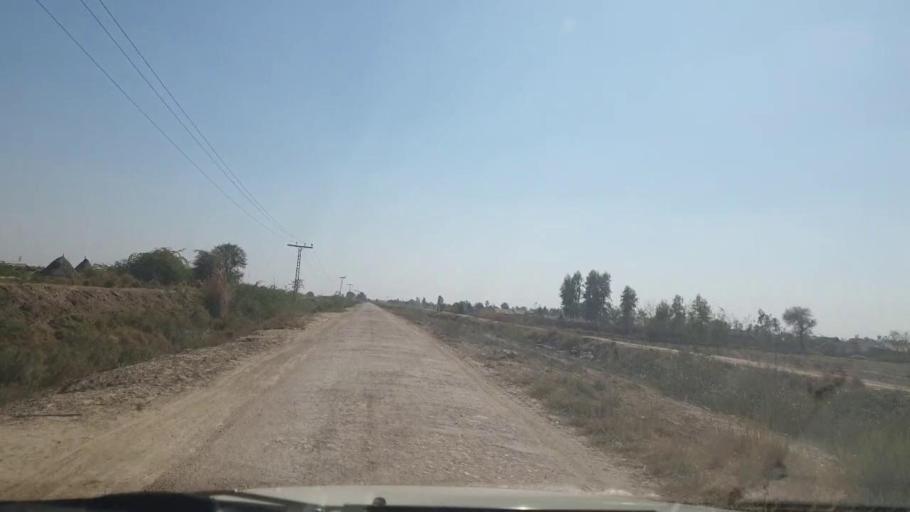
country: PK
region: Sindh
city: Mirpur Khas
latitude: 25.5031
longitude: 69.1352
